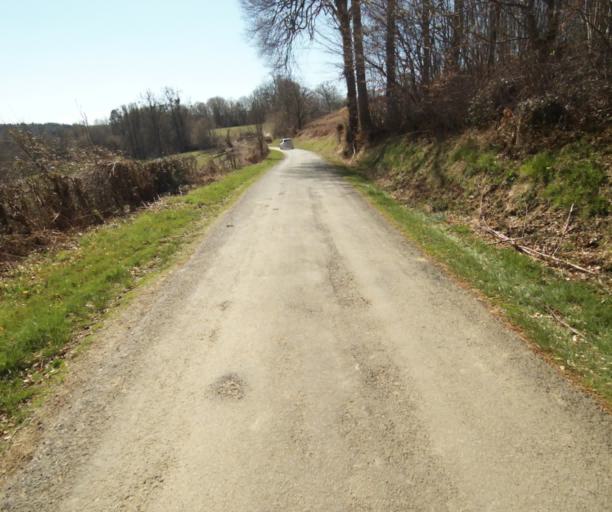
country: FR
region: Limousin
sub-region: Departement de la Correze
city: Saint-Clement
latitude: 45.3214
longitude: 1.7032
